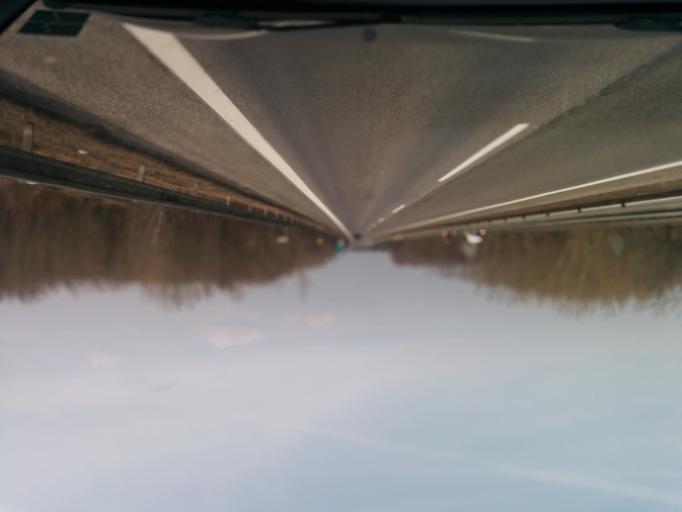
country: SK
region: Trnavsky
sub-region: Okres Galanta
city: Galanta
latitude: 48.2612
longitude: 17.7853
